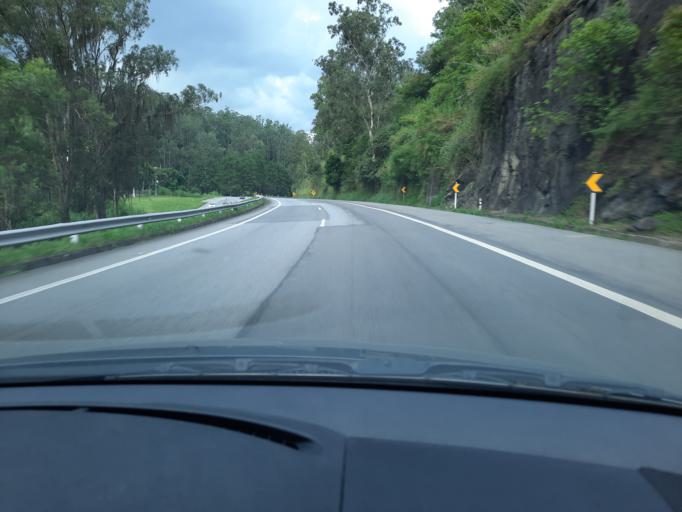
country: BR
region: Rio de Janeiro
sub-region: Petropolis
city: Petropolis
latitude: -22.4368
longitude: -43.1755
